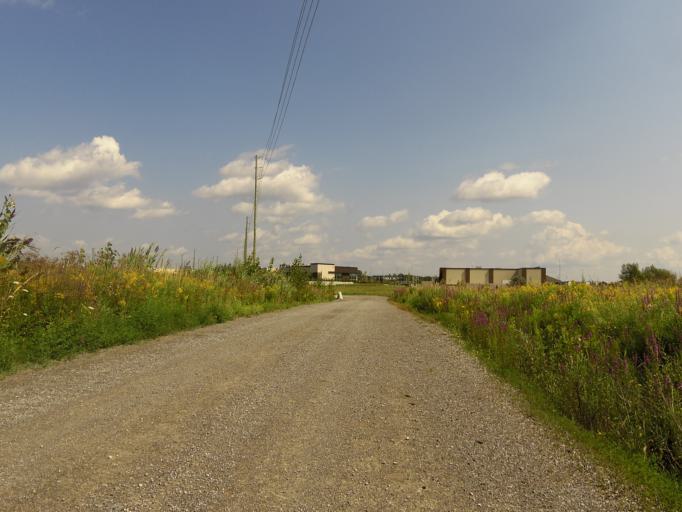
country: CA
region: Ontario
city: Bells Corners
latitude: 45.3055
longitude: -75.9260
